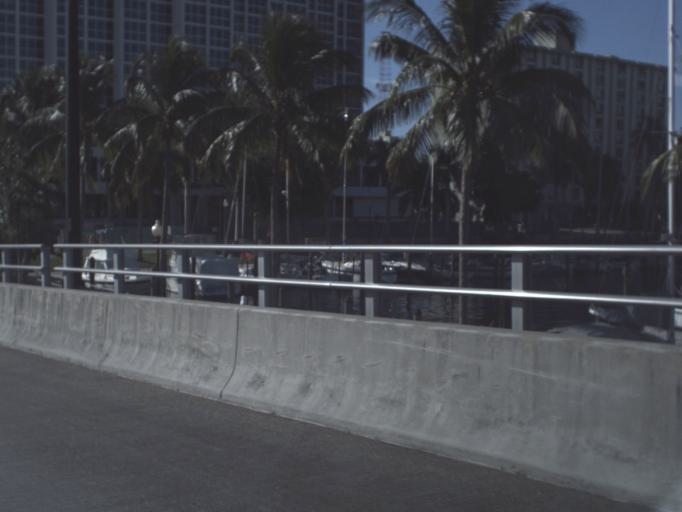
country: US
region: Florida
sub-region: Lee County
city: North Fort Myers
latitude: 26.6486
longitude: -81.8675
